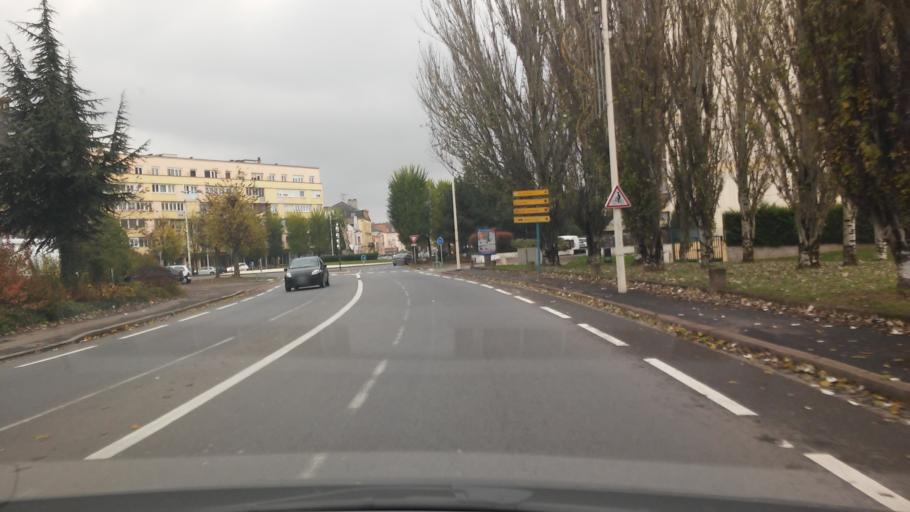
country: FR
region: Lorraine
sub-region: Departement de la Moselle
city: Thionville
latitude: 49.3508
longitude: 6.1603
